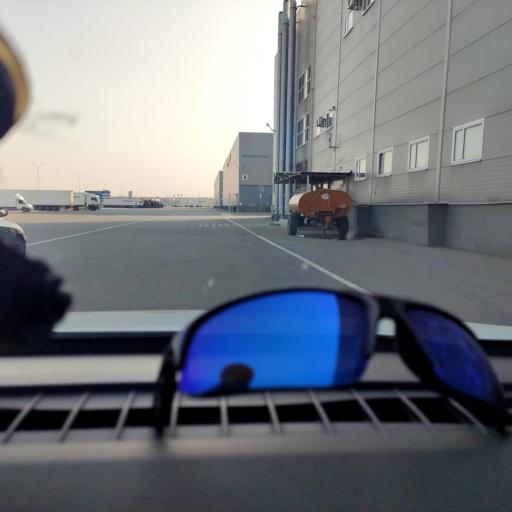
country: RU
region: Samara
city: Samara
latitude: 53.0968
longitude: 50.1338
